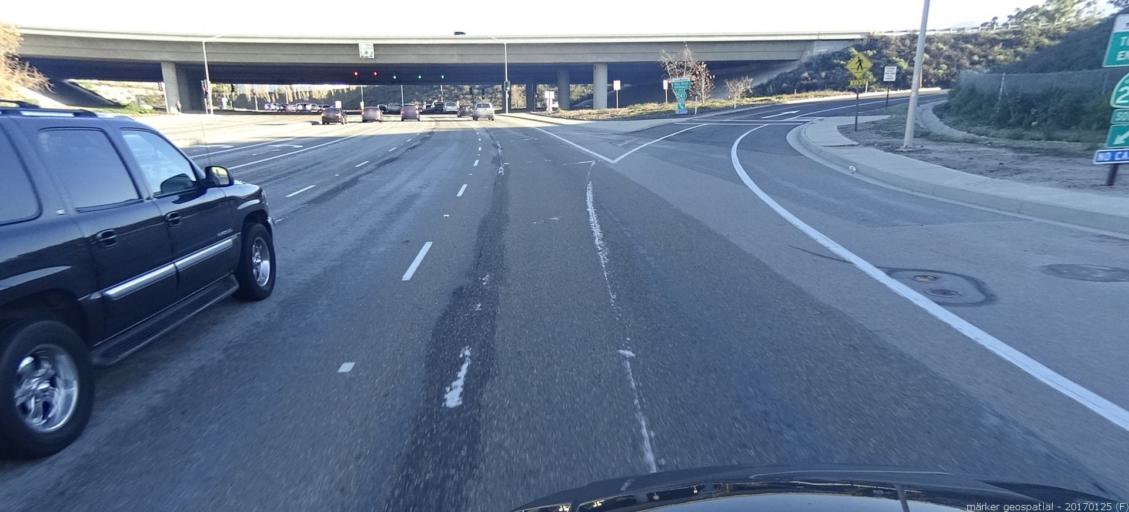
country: US
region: California
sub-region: Orange County
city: Foothill Ranch
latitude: 33.6668
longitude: -117.6512
